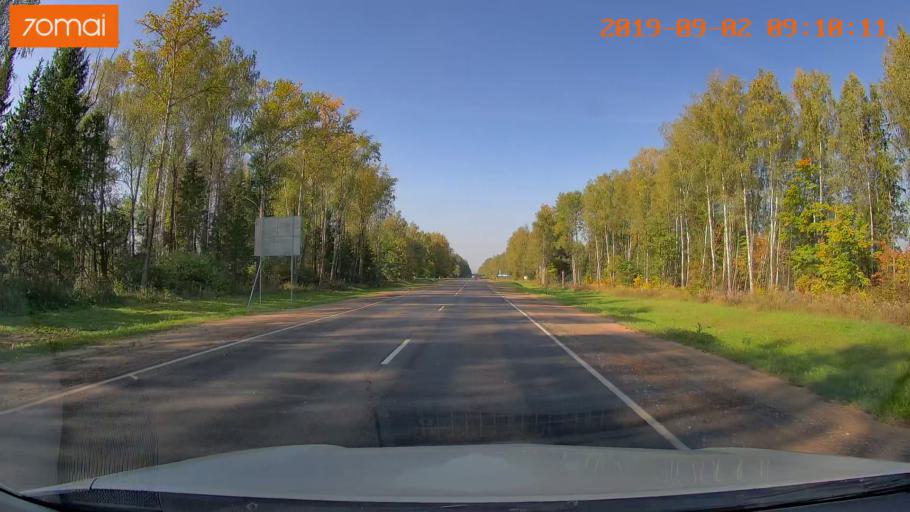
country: RU
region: Kaluga
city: Myatlevo
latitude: 54.8780
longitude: 35.6063
